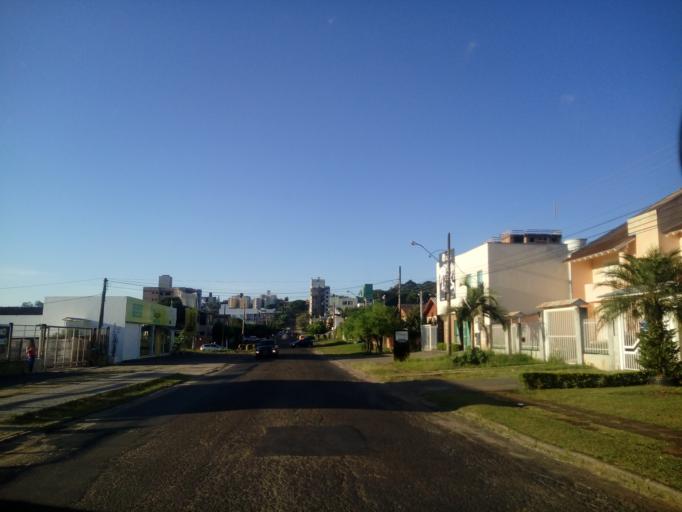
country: BR
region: Santa Catarina
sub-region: Chapeco
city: Chapeco
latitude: -27.1097
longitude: -52.6079
